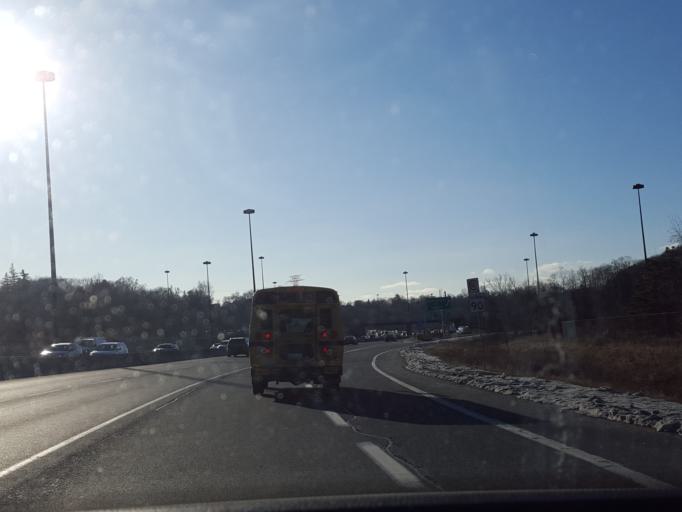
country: CA
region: Ontario
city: Toronto
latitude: 43.7022
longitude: -79.3336
